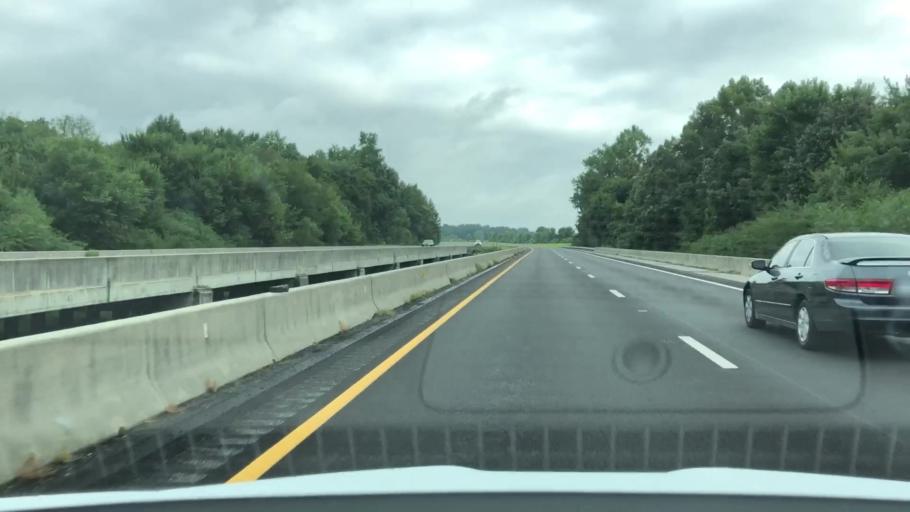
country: US
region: North Carolina
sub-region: Wayne County
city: Fremont
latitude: 35.5150
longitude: -77.9938
